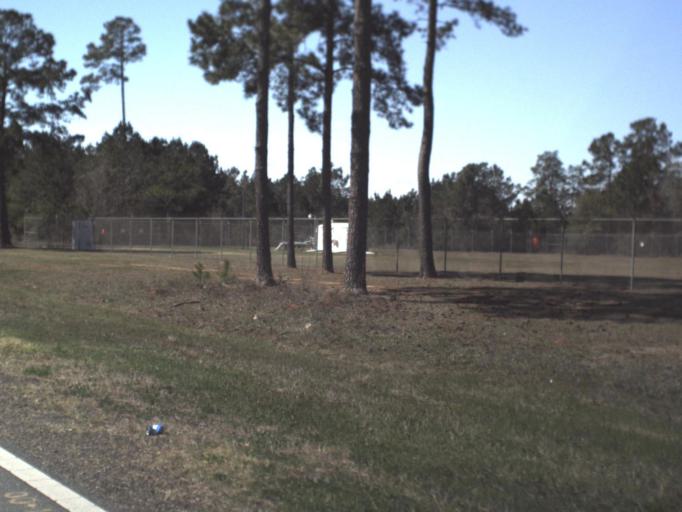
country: US
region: Florida
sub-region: Gadsden County
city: Chattahoochee
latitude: 30.7008
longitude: -84.8041
